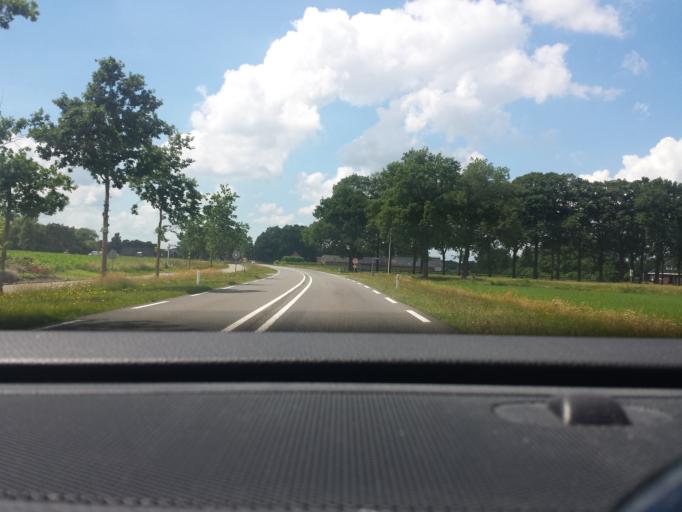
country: NL
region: Overijssel
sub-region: Gemeente Haaksbergen
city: Haaksbergen
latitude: 52.1816
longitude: 6.6918
